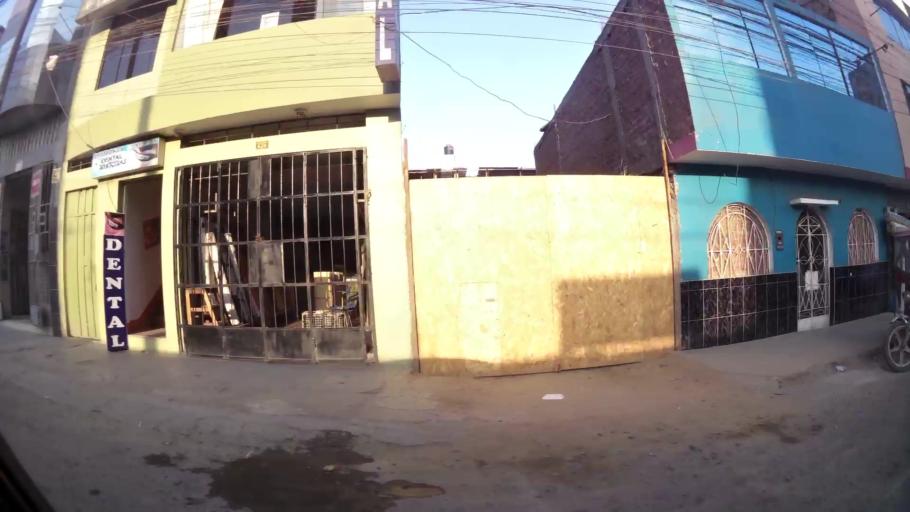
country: PE
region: La Libertad
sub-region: Provincia de Trujillo
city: El Porvenir
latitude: -8.0820
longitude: -79.0007
